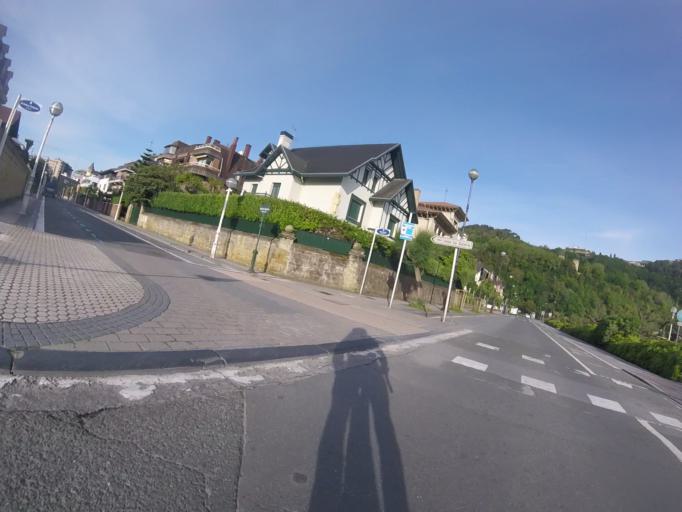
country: ES
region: Basque Country
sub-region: Provincia de Guipuzcoa
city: San Sebastian
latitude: 43.3161
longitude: -2.0033
